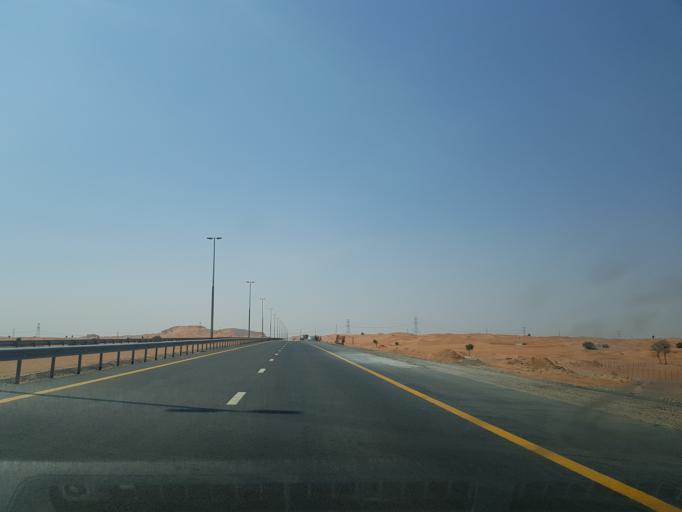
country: AE
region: Ash Shariqah
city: Adh Dhayd
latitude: 25.2440
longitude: 55.8620
